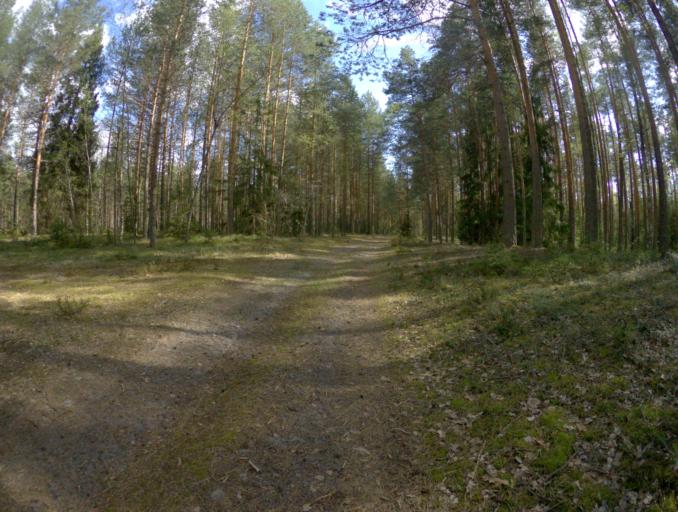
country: RU
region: Vladimir
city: Golovino
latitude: 55.8925
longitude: 40.3877
